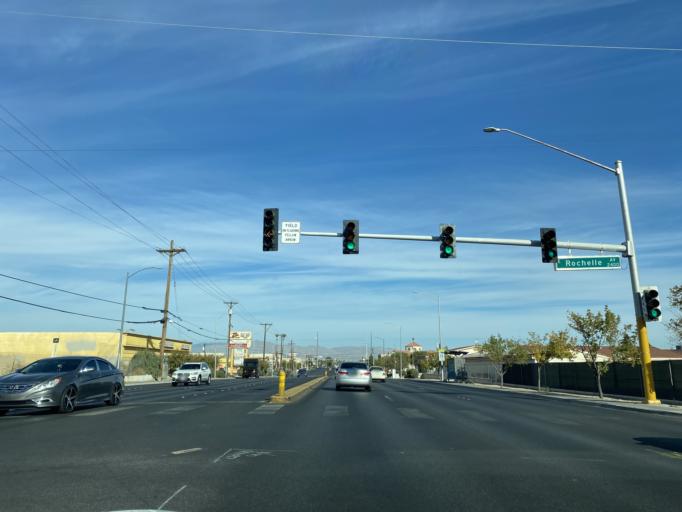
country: US
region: Nevada
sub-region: Clark County
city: Winchester
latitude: 36.1110
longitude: -115.1191
